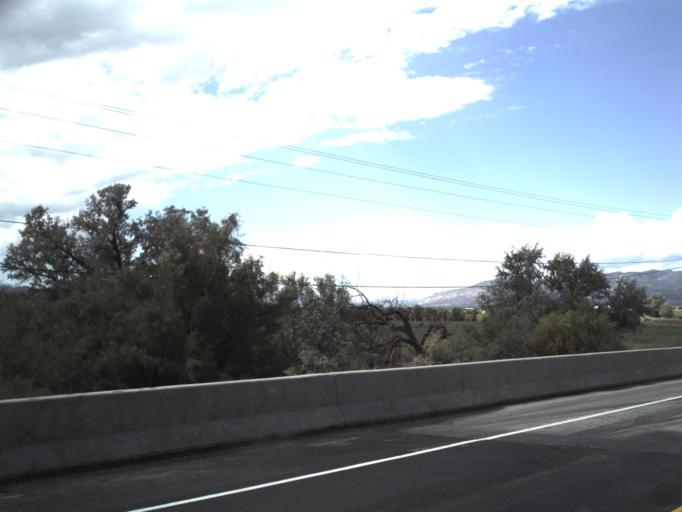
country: US
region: Utah
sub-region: Sevier County
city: Salina
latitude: 38.9549
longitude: -111.8842
